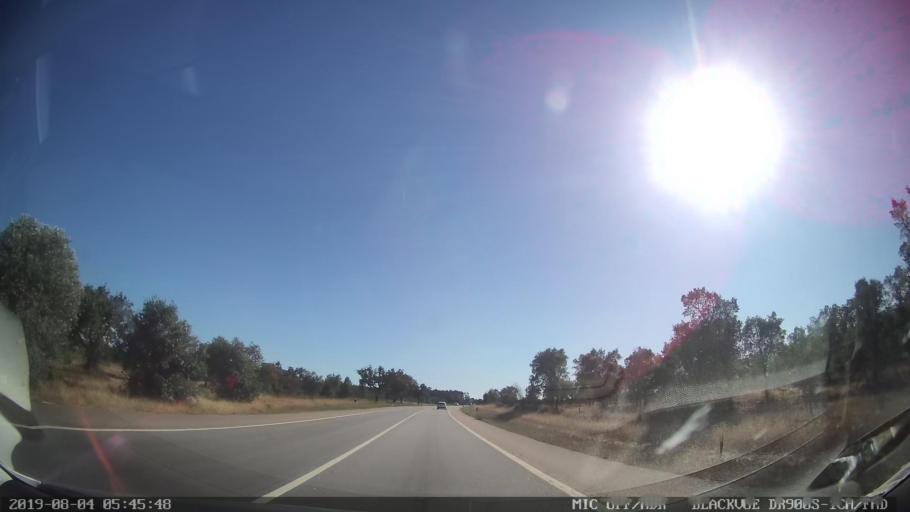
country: PT
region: Portalegre
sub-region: Nisa
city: Nisa
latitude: 39.4587
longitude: -7.7790
